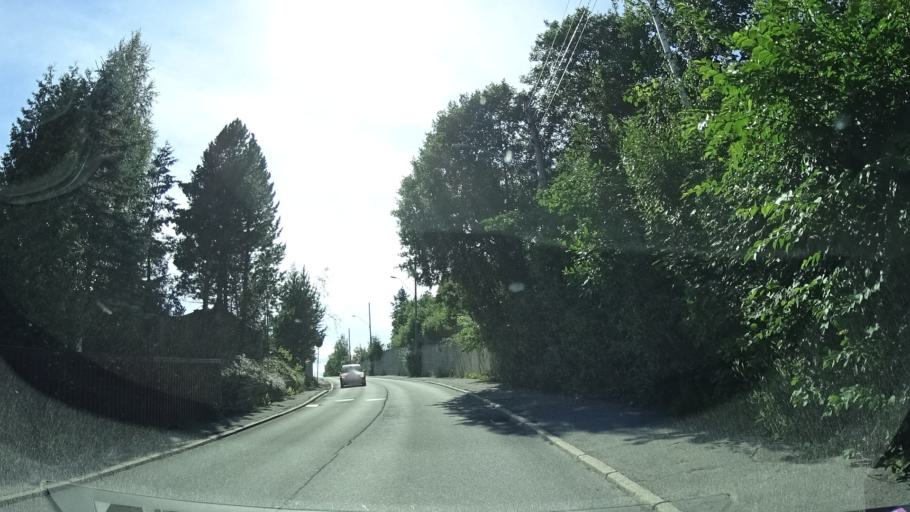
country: NO
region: Oslo
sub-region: Oslo
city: Sjolyststranda
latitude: 59.9590
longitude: 10.6776
